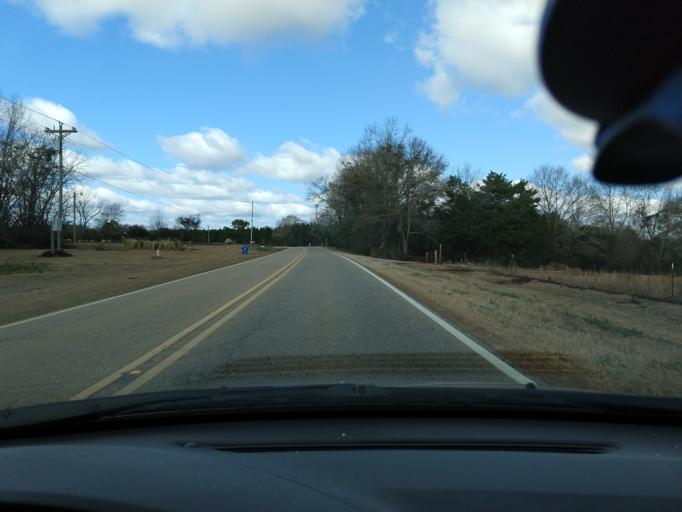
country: US
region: Alabama
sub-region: Coffee County
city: New Brockton
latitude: 31.3153
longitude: -85.9332
